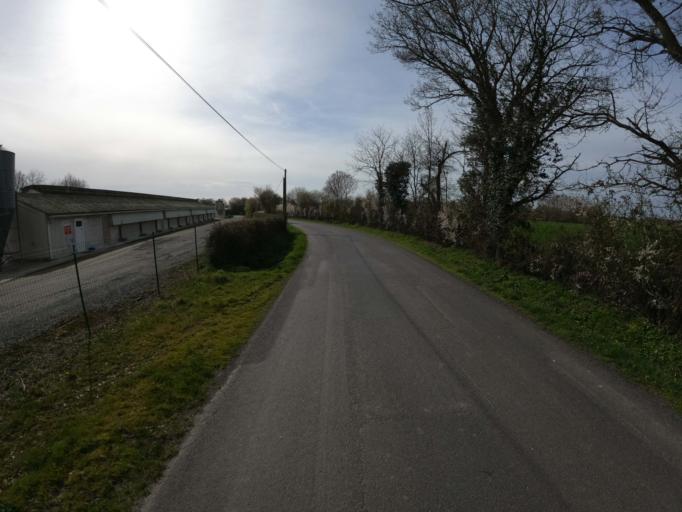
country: FR
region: Pays de la Loire
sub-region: Departement de la Vendee
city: Bouffere
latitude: 46.9540
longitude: -1.3644
